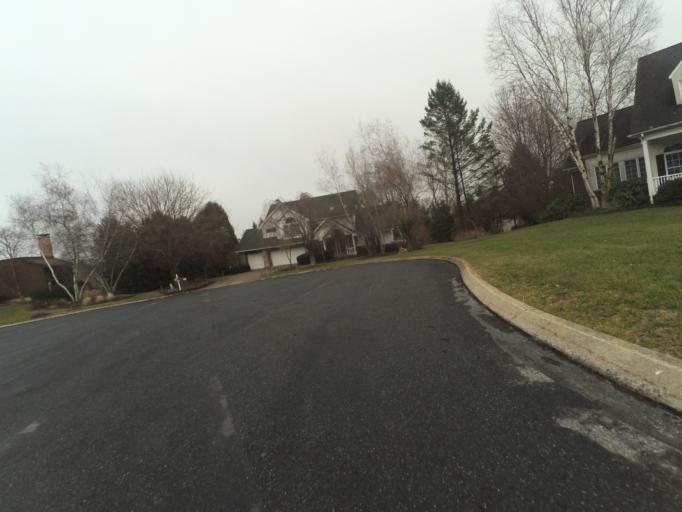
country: US
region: Pennsylvania
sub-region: Centre County
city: Park Forest Village
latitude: 40.7877
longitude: -77.9119
